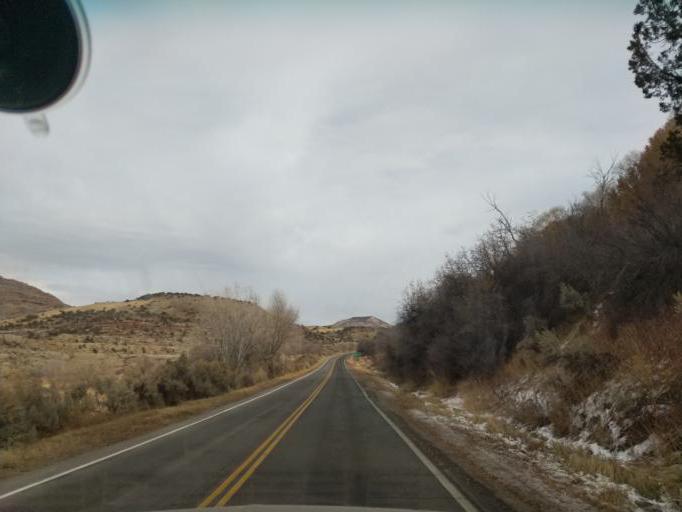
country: US
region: Colorado
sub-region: Mesa County
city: Palisade
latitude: 39.1871
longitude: -108.1354
